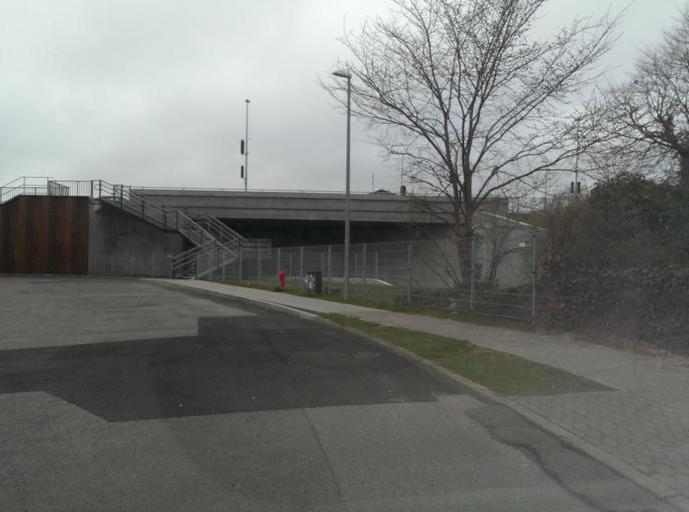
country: DK
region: South Denmark
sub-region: Esbjerg Kommune
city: Esbjerg
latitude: 55.4748
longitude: 8.4812
